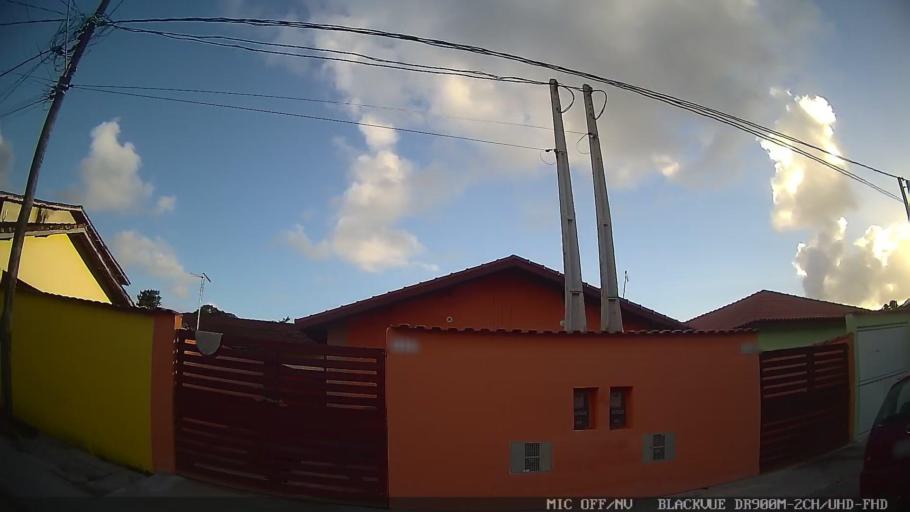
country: BR
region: Sao Paulo
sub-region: Itanhaem
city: Itanhaem
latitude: -24.1397
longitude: -46.7281
